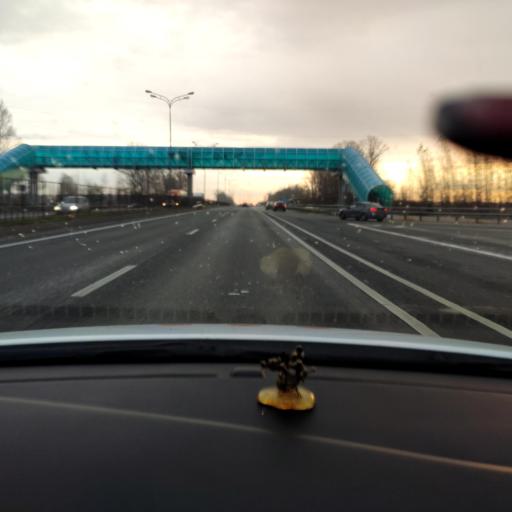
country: RU
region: Tatarstan
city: Aysha
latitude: 55.8711
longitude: 48.6679
